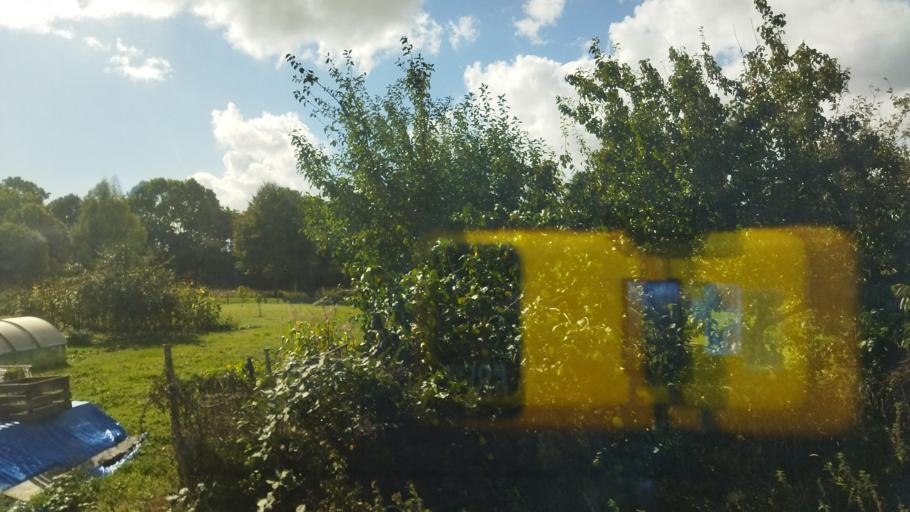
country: DE
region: Lower Saxony
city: Emden
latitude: 53.3507
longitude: 7.2383
